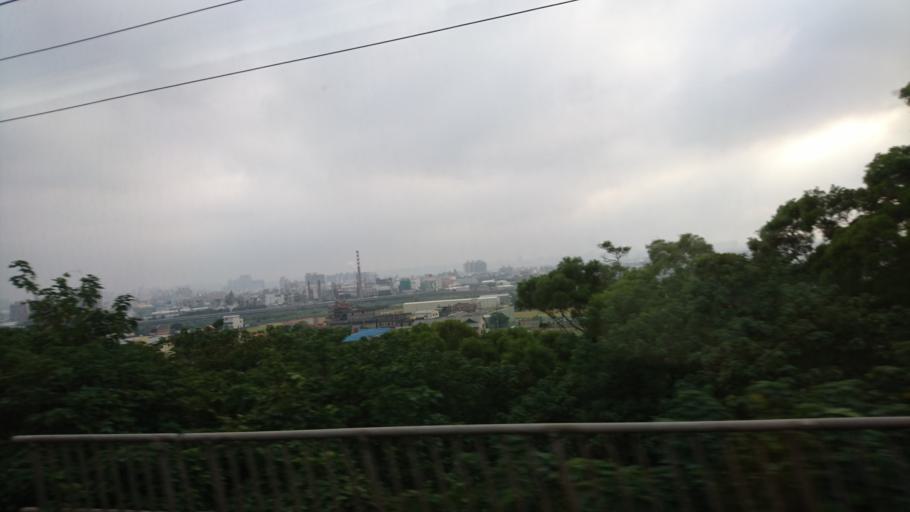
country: TW
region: Taiwan
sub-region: Hsinchu
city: Zhubei
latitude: 24.8585
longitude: 121.0002
